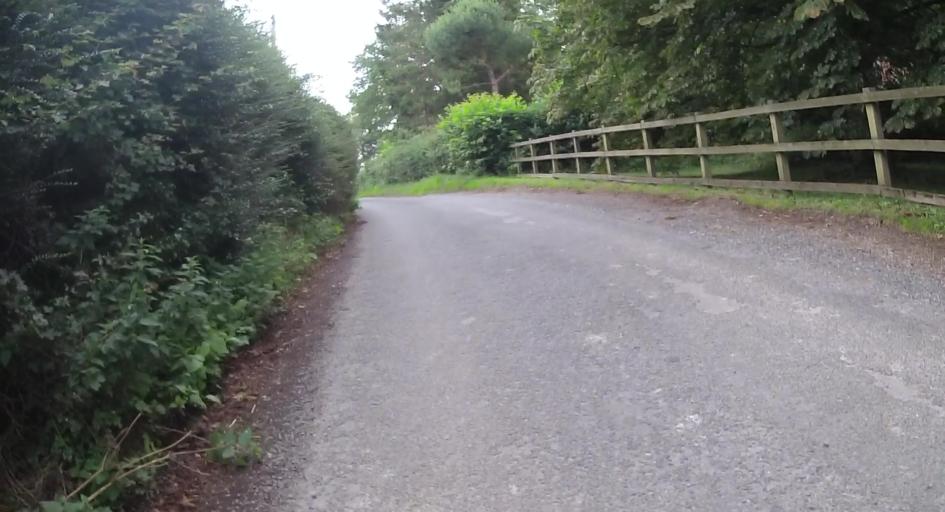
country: GB
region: England
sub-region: Hampshire
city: Four Marks
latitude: 51.1541
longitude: -1.0941
